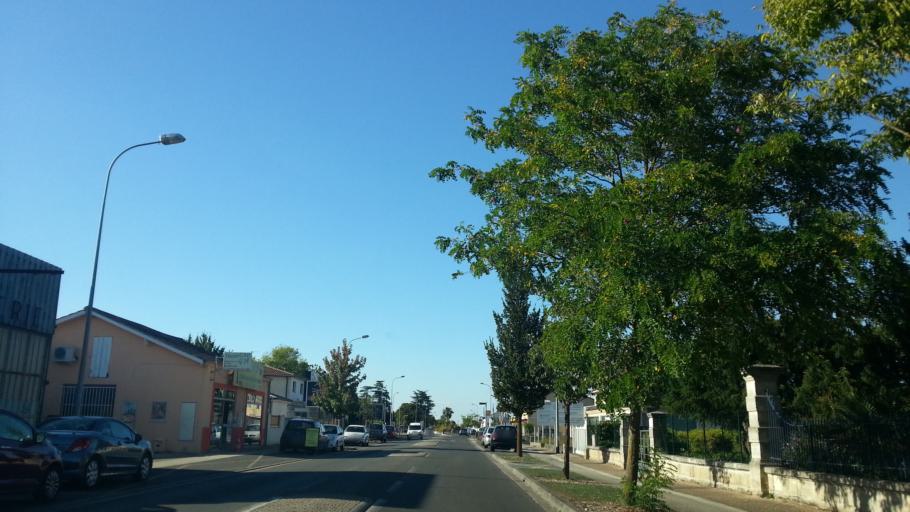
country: FR
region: Aquitaine
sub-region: Departement de la Gironde
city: Villenave-d'Ornon
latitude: 44.7698
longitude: -0.5639
